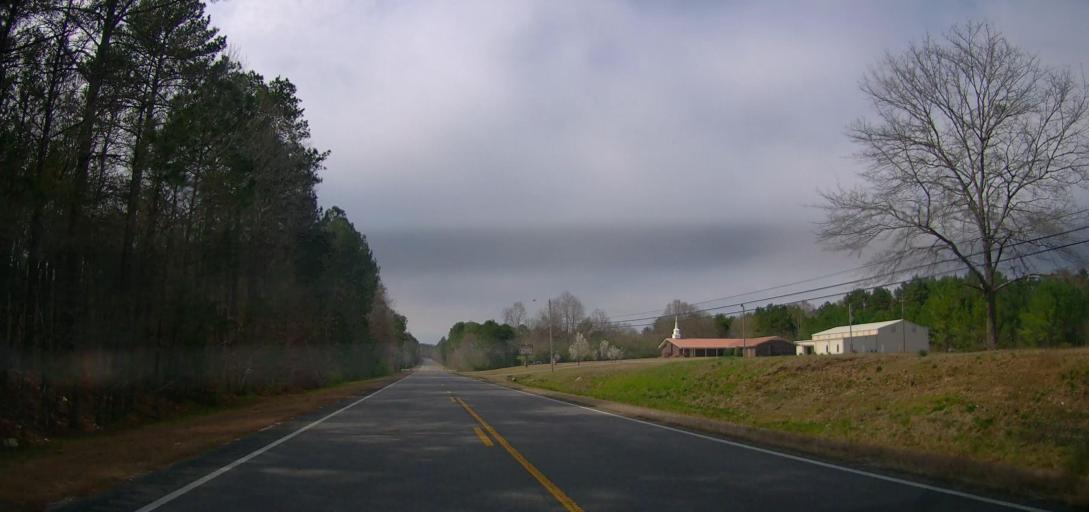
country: US
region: Alabama
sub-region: Walker County
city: Carbon Hill
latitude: 33.9074
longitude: -87.5546
